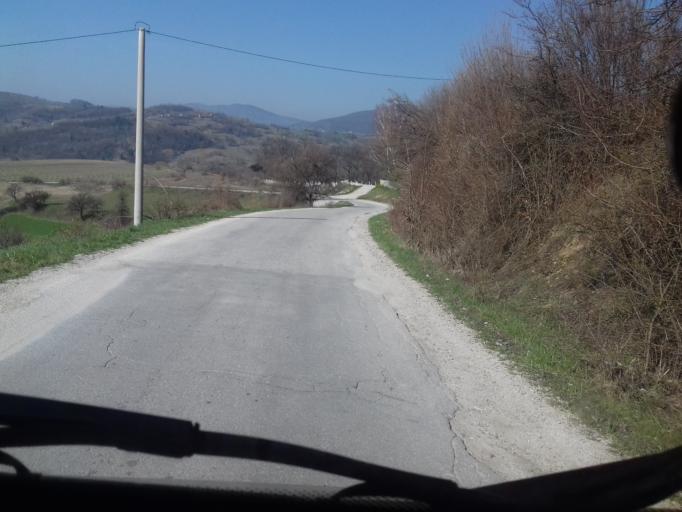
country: BA
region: Federation of Bosnia and Herzegovina
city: Vitez
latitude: 44.2403
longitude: 17.7693
